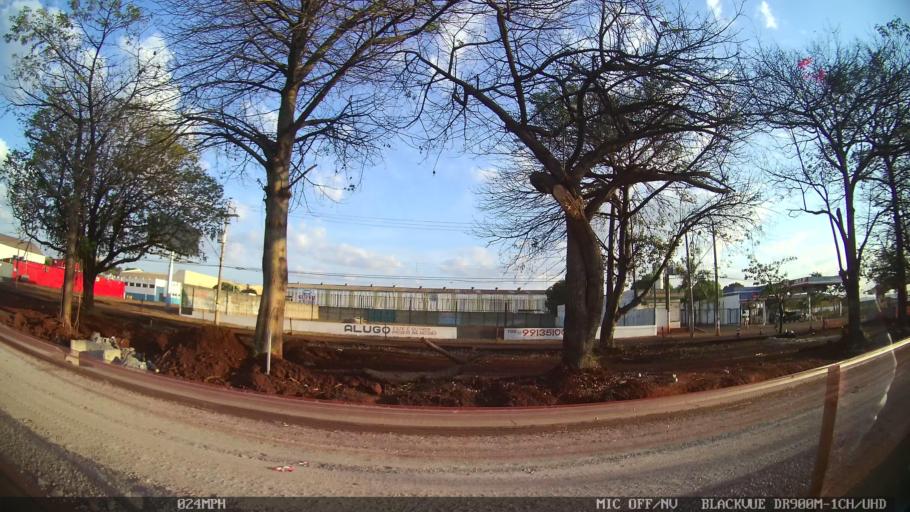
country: BR
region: Sao Paulo
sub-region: Ribeirao Preto
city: Ribeirao Preto
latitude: -21.1408
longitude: -47.7853
